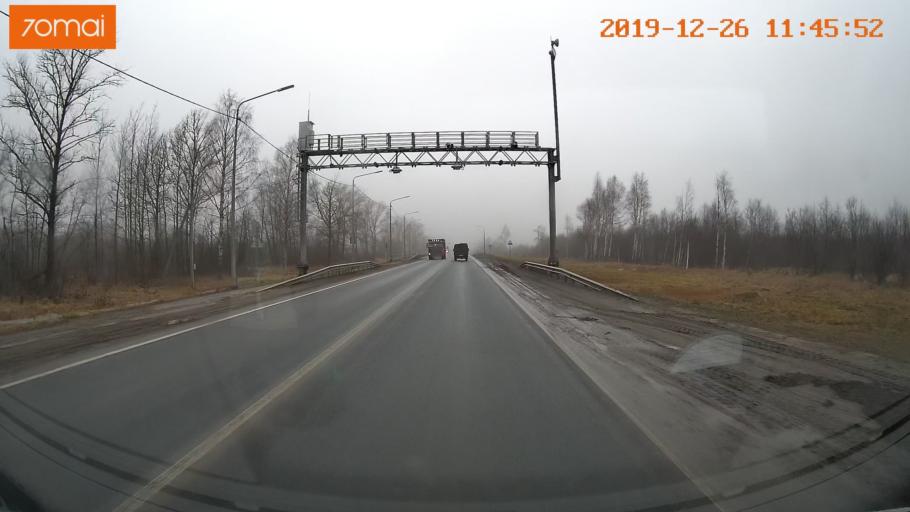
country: RU
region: Vologda
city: Sheksna
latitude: 59.2212
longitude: 38.4783
